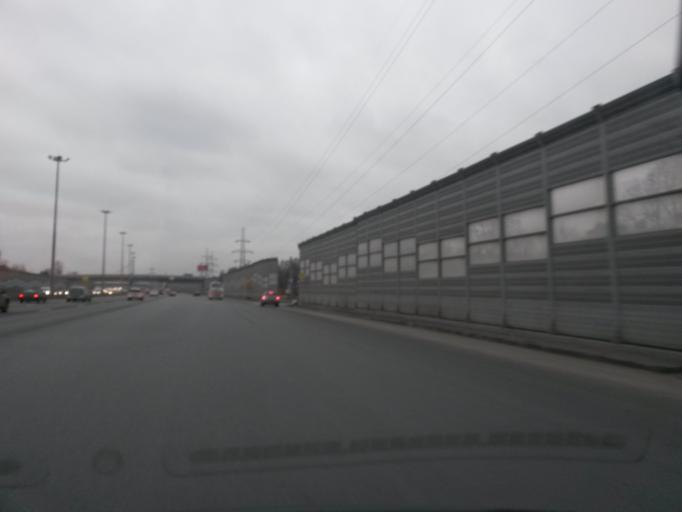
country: RU
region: Moskovskaya
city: Druzhba
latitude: 55.8875
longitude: 37.7366
